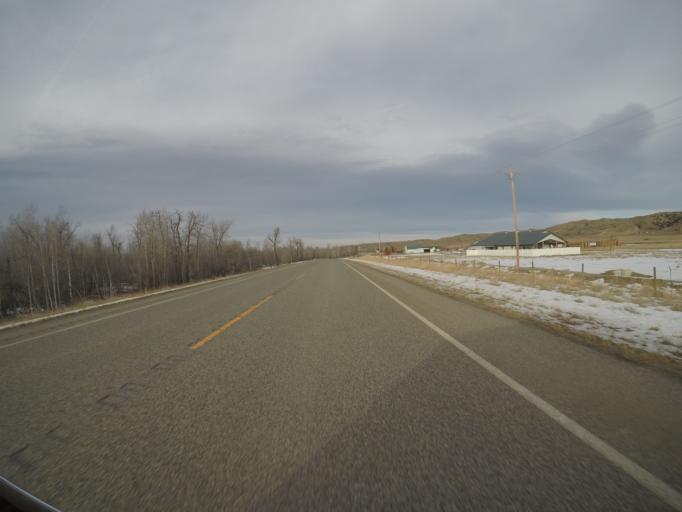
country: US
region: Montana
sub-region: Stillwater County
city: Absarokee
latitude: 45.4585
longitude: -109.4489
